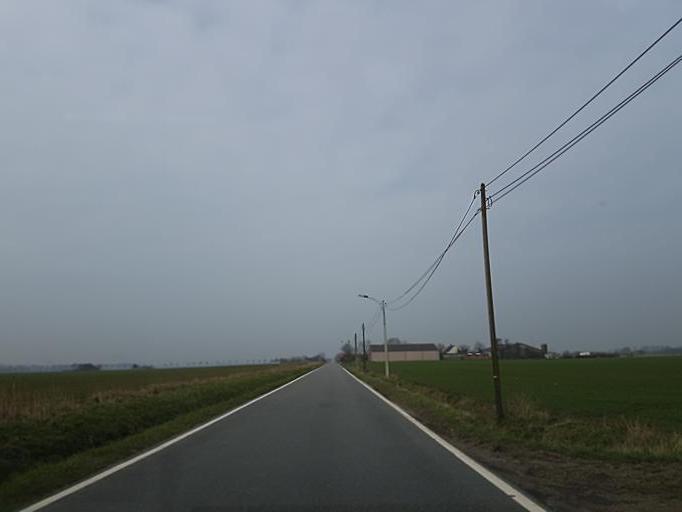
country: BE
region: Flanders
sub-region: Provincie Oost-Vlaanderen
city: Beveren
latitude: 51.3019
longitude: 4.2315
